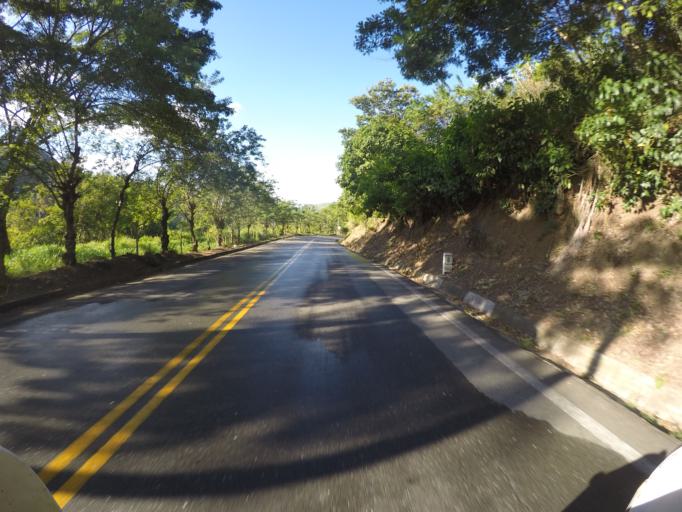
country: CO
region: Valle del Cauca
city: Cartago
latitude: 4.7174
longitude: -75.8607
